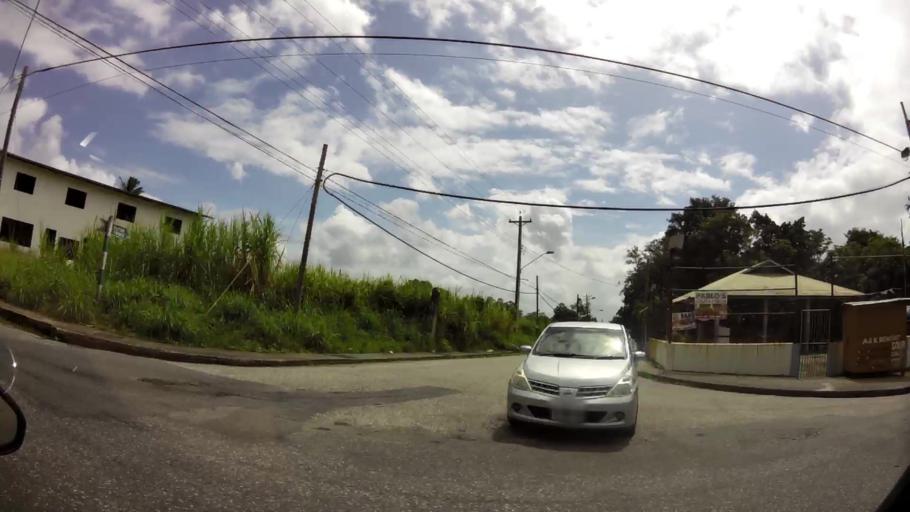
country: TT
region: Borough of Arima
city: Arima
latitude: 10.6335
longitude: -61.2944
